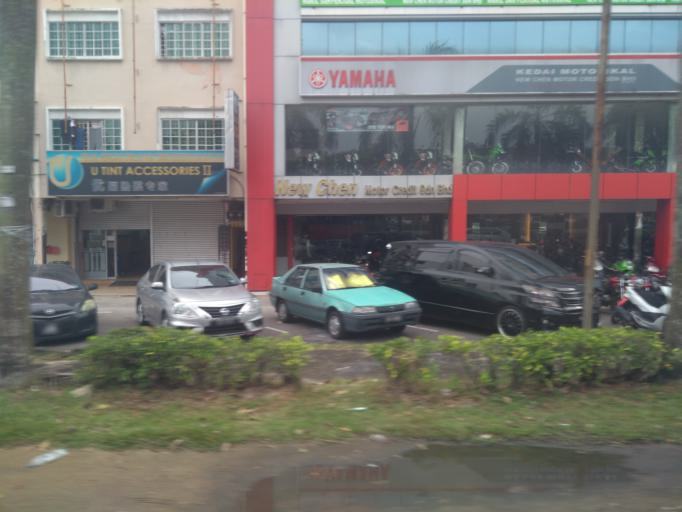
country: MY
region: Johor
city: Johor Bahru
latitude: 1.4892
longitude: 103.7118
